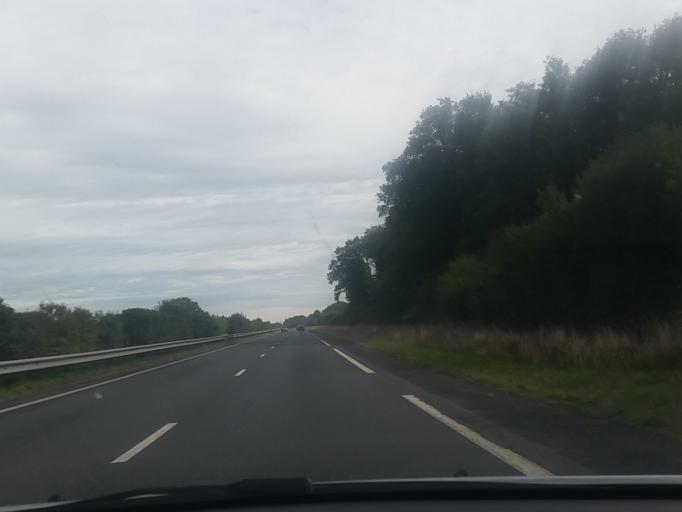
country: FR
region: Pays de la Loire
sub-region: Departement de la Loire-Atlantique
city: Chateaubriant
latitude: 47.6881
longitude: -1.4317
